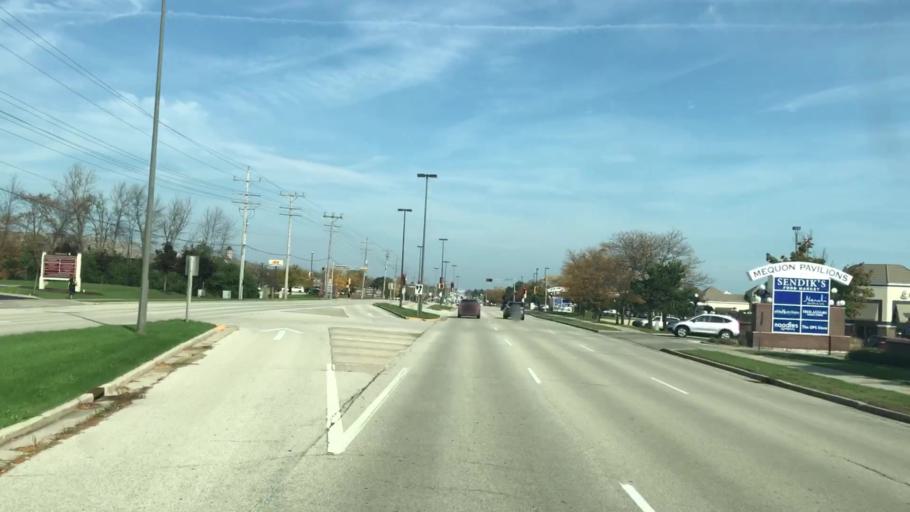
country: US
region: Wisconsin
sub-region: Milwaukee County
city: River Hills
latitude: 43.2166
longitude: -87.9241
